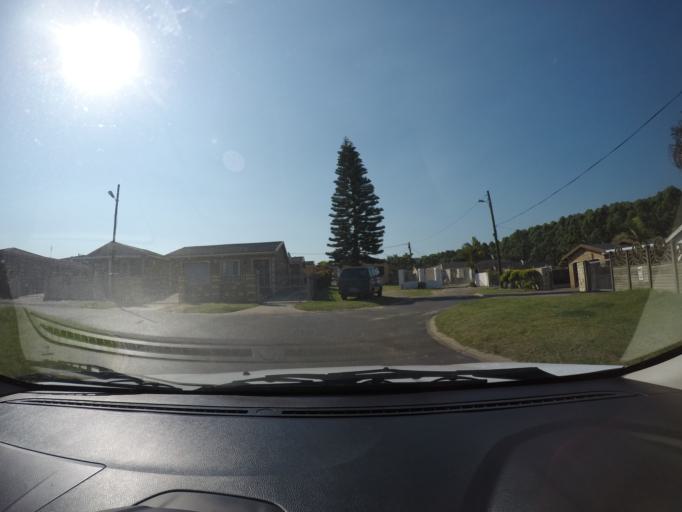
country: ZA
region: KwaZulu-Natal
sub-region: uThungulu District Municipality
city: Richards Bay
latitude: -28.7163
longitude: 32.0439
